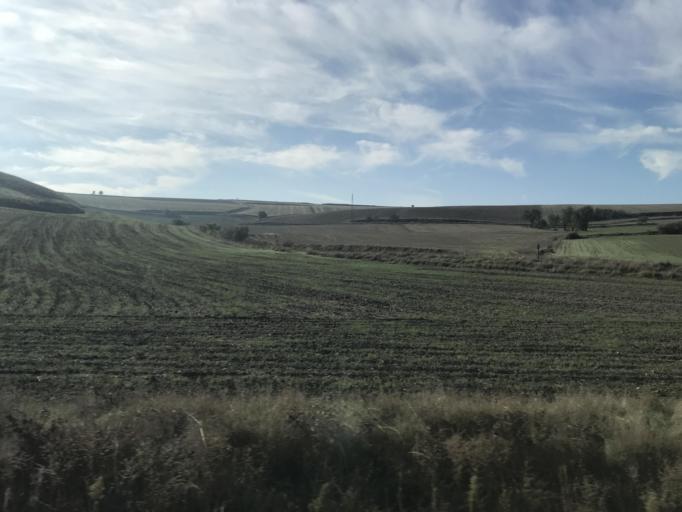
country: ES
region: Castille and Leon
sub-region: Provincia de Burgos
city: Cubo de Bureba
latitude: 42.6244
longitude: -3.1998
